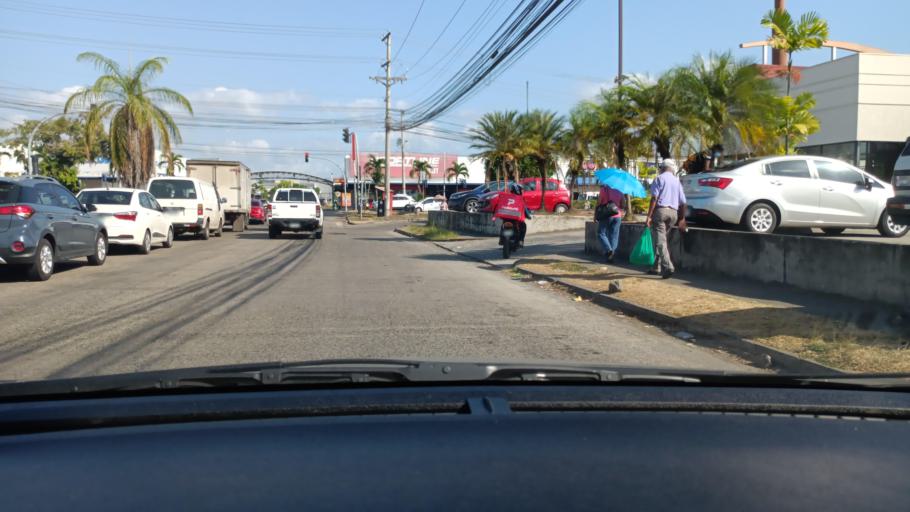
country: PA
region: Panama
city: San Miguelito
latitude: 9.0447
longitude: -79.4506
